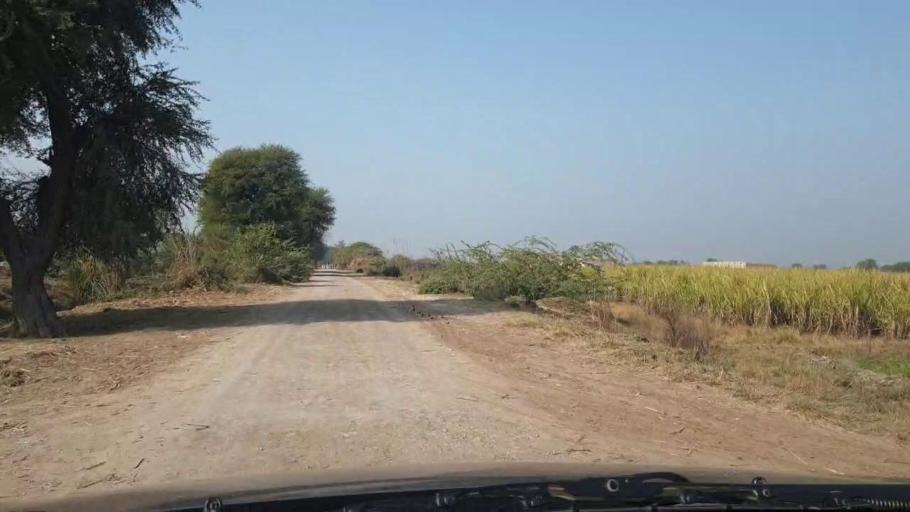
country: PK
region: Sindh
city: Jhol
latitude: 25.9603
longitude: 68.9329
